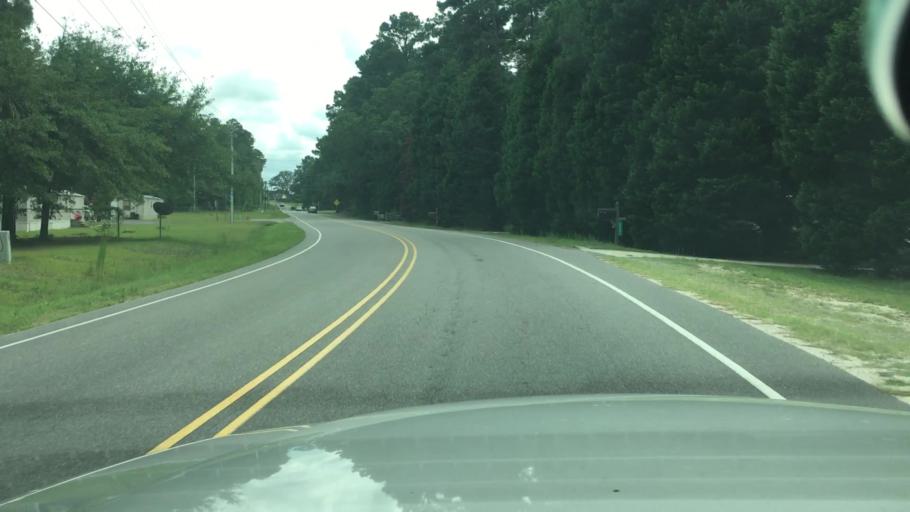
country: US
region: North Carolina
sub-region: Hoke County
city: Rockfish
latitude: 35.0073
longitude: -79.0236
